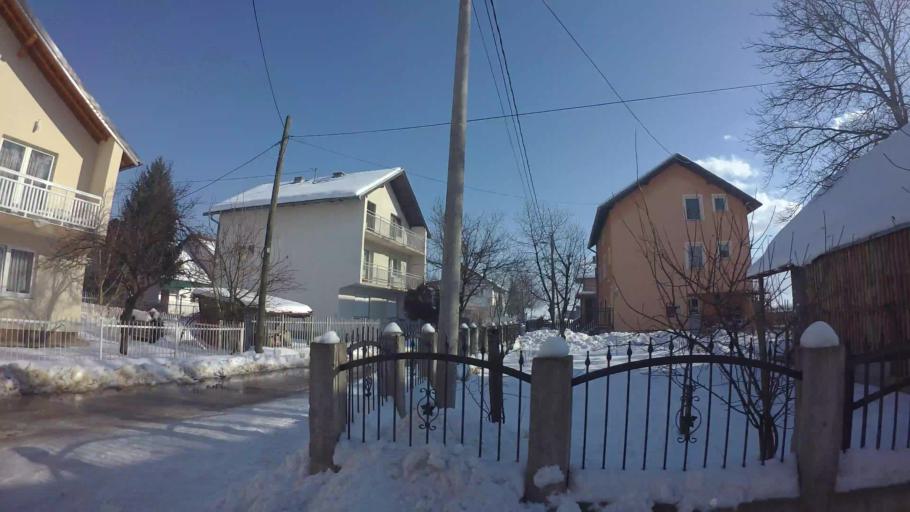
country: BA
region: Federation of Bosnia and Herzegovina
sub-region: Kanton Sarajevo
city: Sarajevo
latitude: 43.8069
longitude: 18.3158
